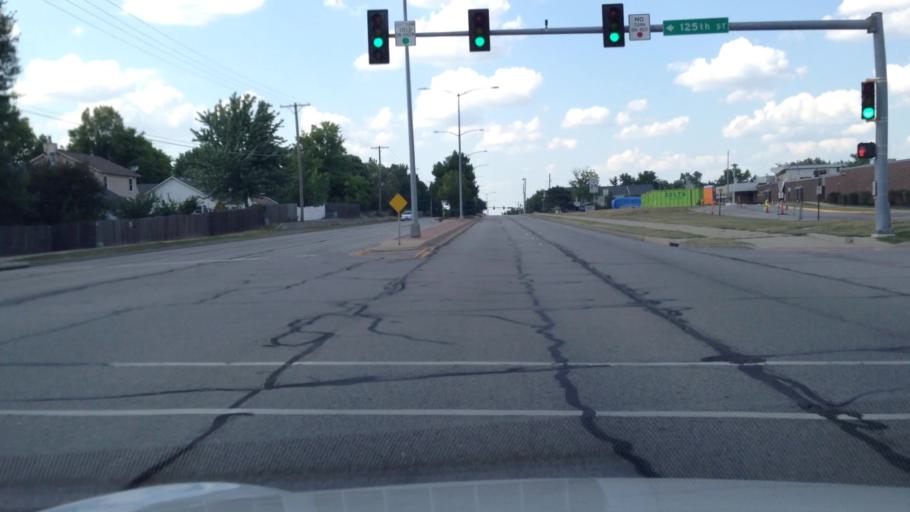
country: US
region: Kansas
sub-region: Johnson County
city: Olathe
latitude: 38.9004
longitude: -94.7973
